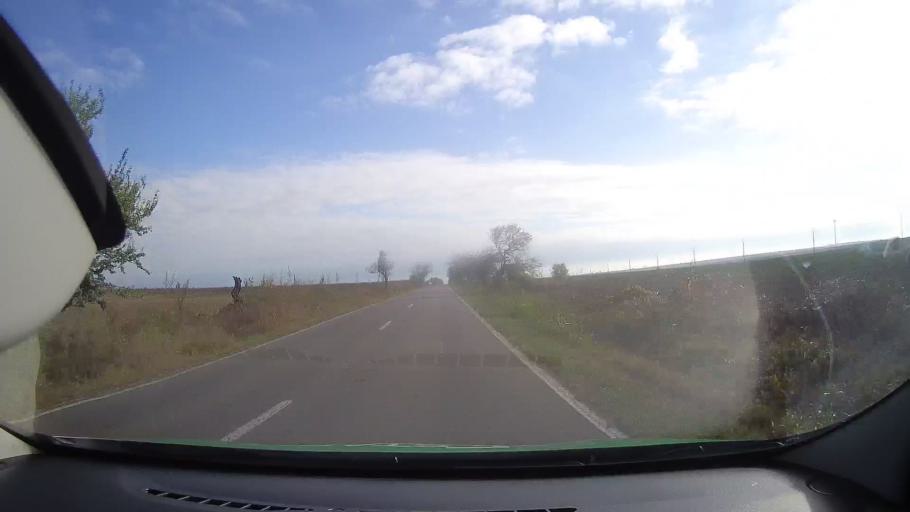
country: RO
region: Tulcea
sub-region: Comuna Mahmudia
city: Mahmudia
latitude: 45.0776
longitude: 29.0621
